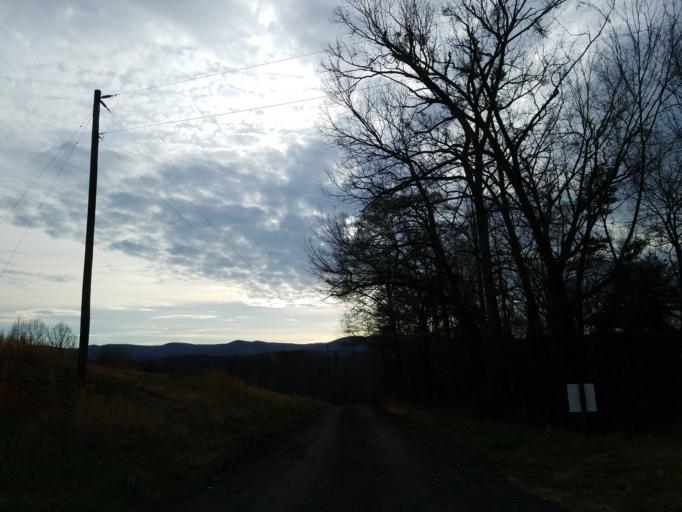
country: US
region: Georgia
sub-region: Dawson County
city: Dawsonville
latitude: 34.5272
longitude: -84.2501
